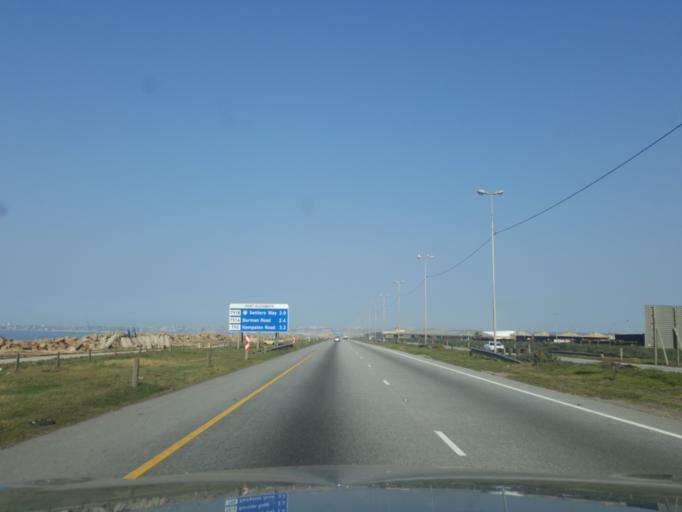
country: ZA
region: Eastern Cape
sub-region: Nelson Mandela Bay Metropolitan Municipality
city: Port Elizabeth
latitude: -33.8947
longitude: 25.6212
